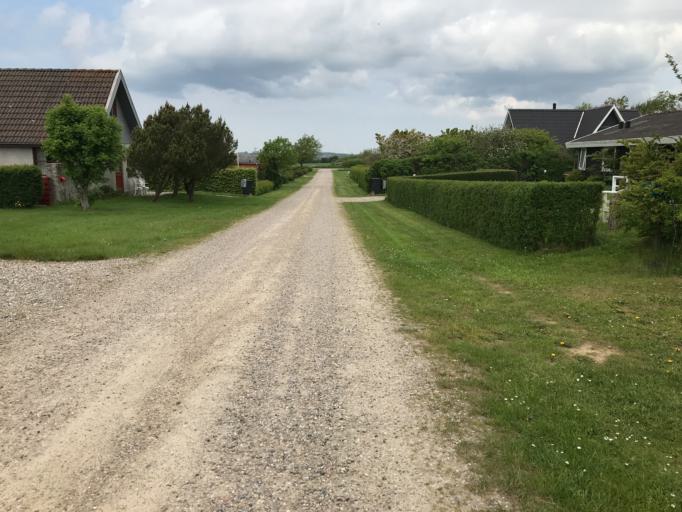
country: DK
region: South Denmark
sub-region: Assens Kommune
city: Assens
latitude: 55.3329
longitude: 9.8799
